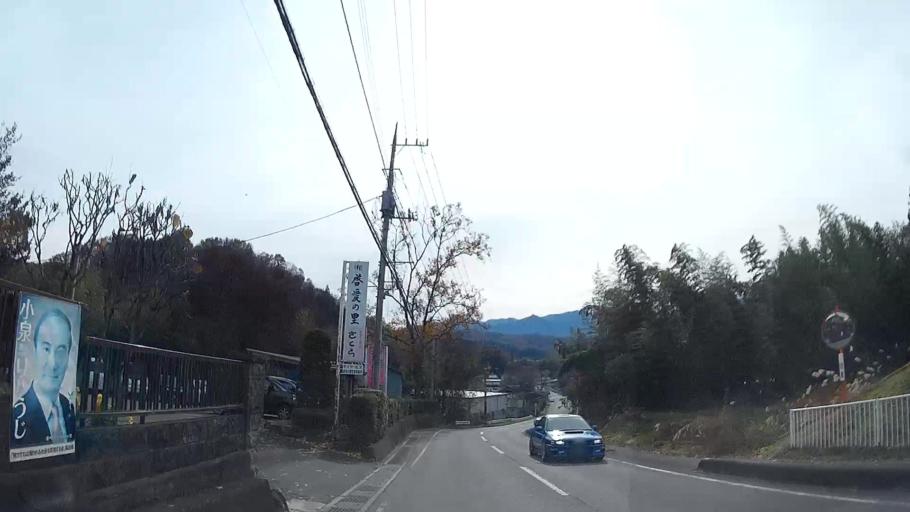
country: JP
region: Saitama
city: Chichibu
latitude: 35.9964
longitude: 139.0327
